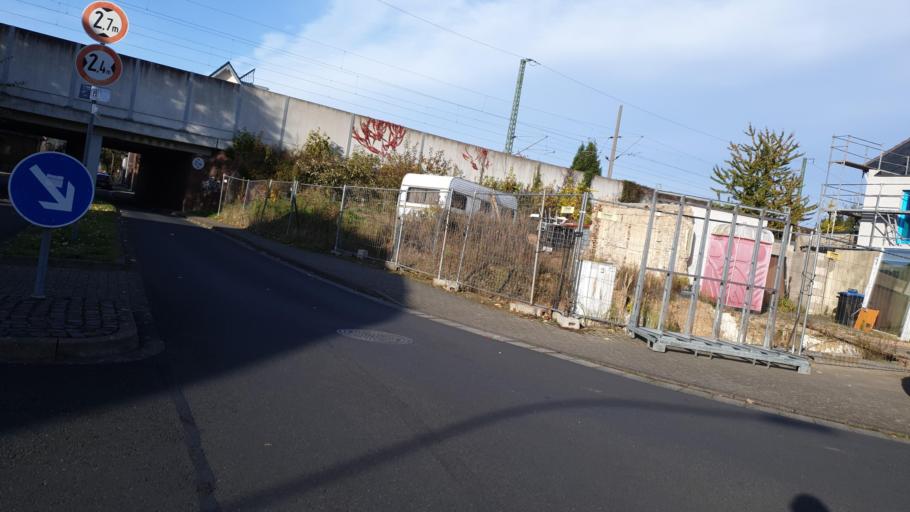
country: DE
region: North Rhine-Westphalia
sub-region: Regierungsbezirk Koln
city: Kerpen
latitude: 50.9012
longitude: 6.6761
